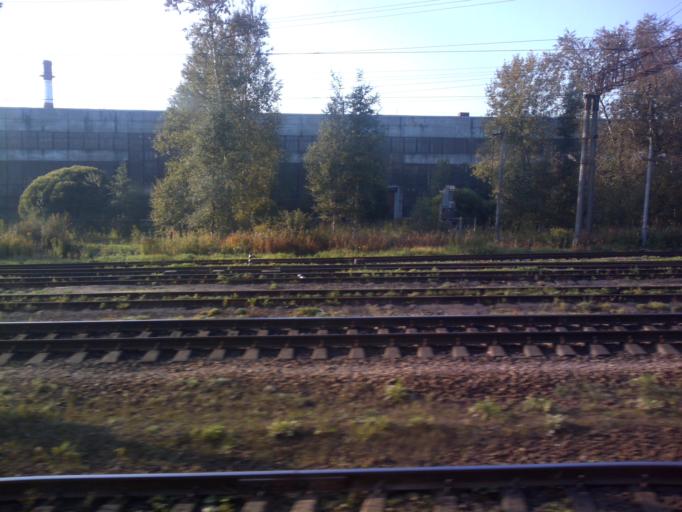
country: RU
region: St.-Petersburg
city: Krasnogvargeisky
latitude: 59.9805
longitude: 30.5194
